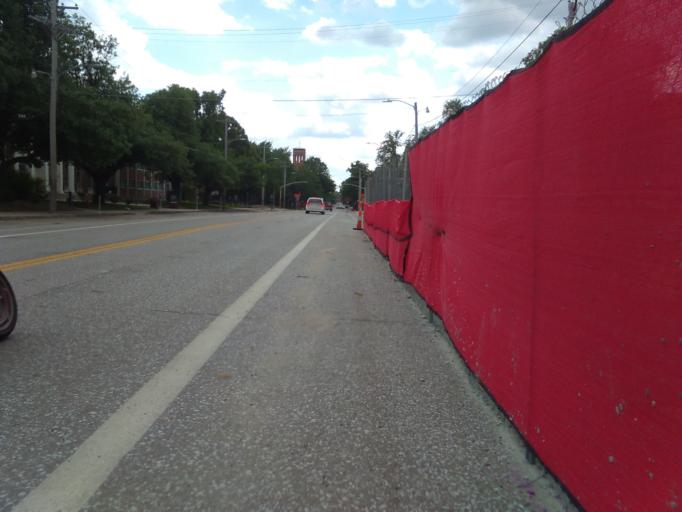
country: US
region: Nebraska
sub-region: Lancaster County
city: Lincoln
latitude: 40.8193
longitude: -96.6982
